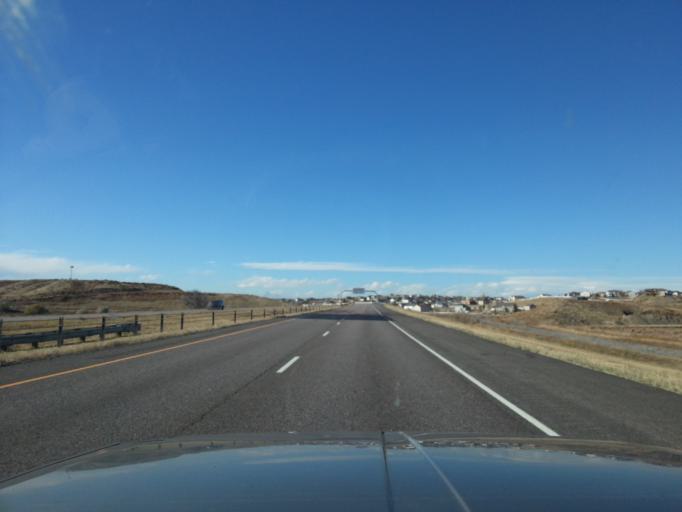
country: US
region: Colorado
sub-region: Adams County
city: Todd Creek
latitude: 39.9491
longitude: -104.8617
